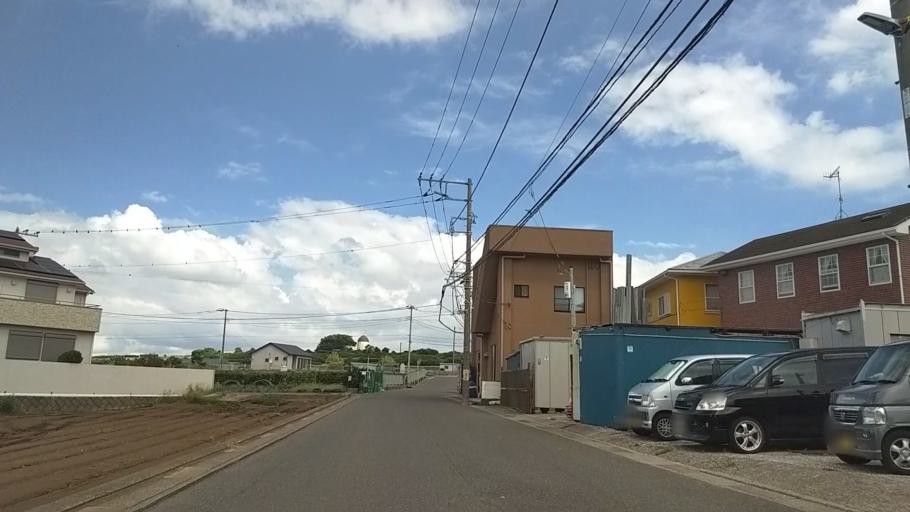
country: JP
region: Kanagawa
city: Miura
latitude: 35.1975
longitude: 139.6100
